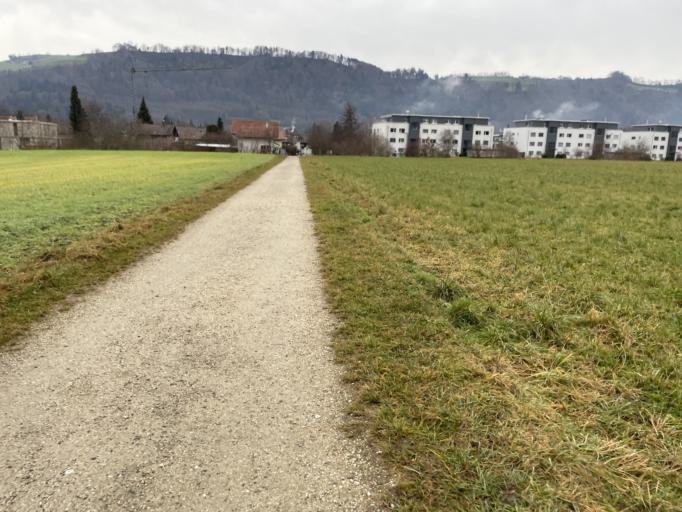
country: CH
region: Bern
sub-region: Bern-Mittelland District
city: Munsingen
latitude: 46.8766
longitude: 7.5524
